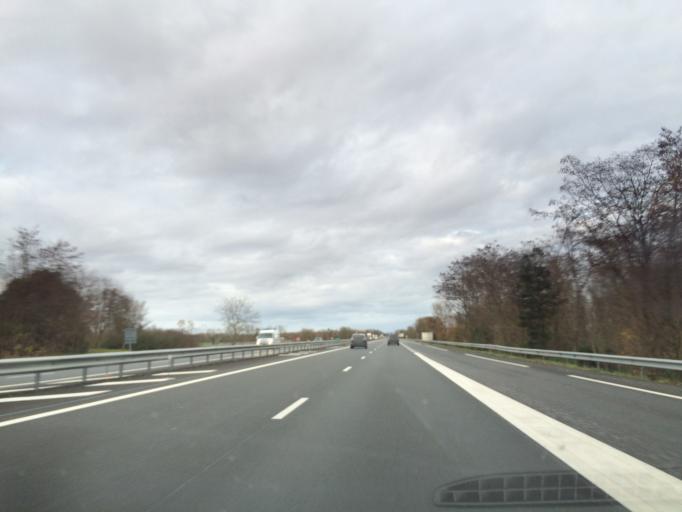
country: FR
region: Poitou-Charentes
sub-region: Departement des Deux-Sevres
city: Fors
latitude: 46.2236
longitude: -0.4475
